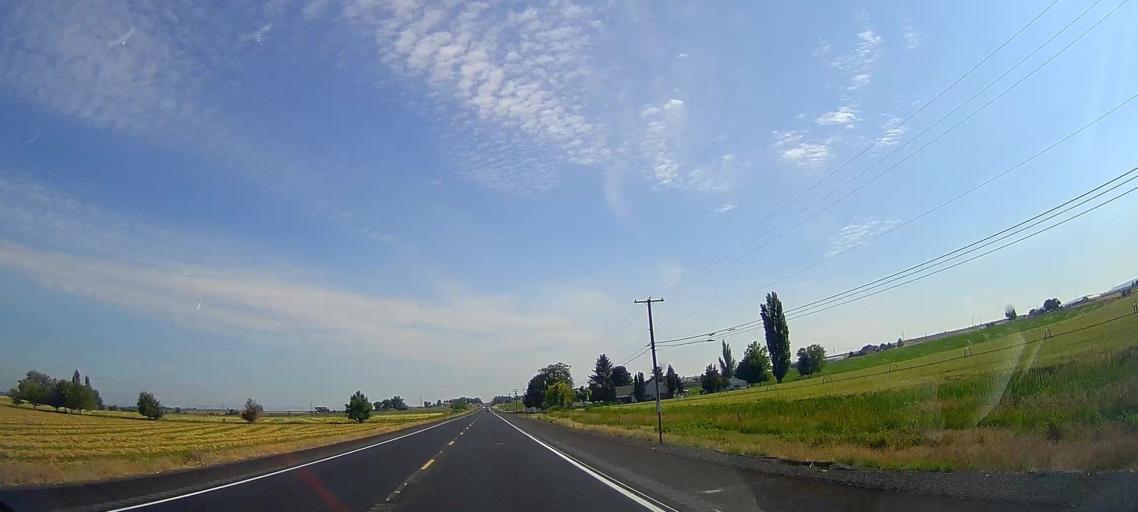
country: US
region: Oregon
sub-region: Jefferson County
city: Culver
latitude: 44.5553
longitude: -121.1671
